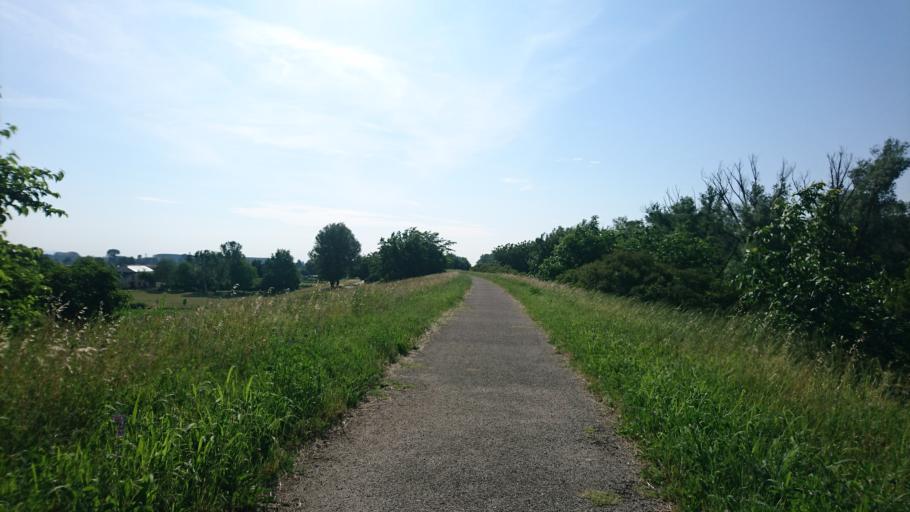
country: IT
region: Veneto
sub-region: Provincia di Verona
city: Villa Bartolomea
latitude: 45.1748
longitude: 11.3340
